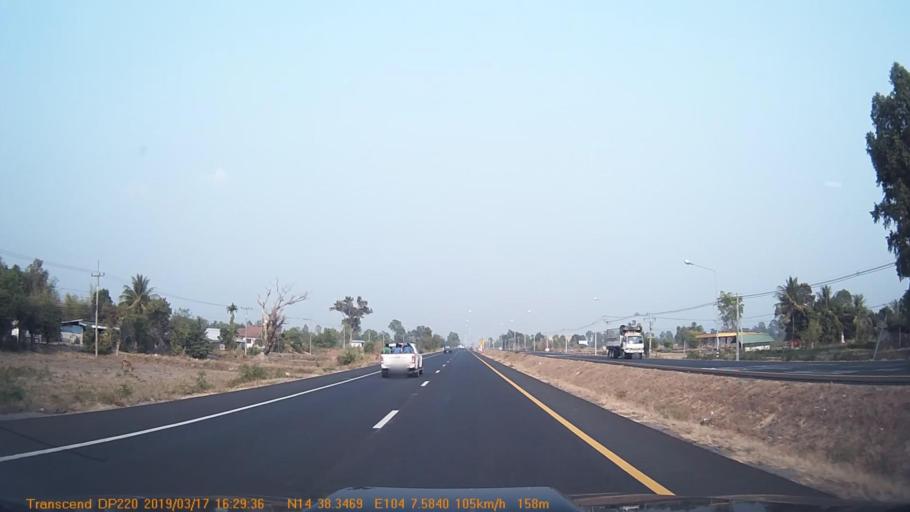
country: TH
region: Sisaket
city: Phu Sing
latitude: 14.6391
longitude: 104.1270
